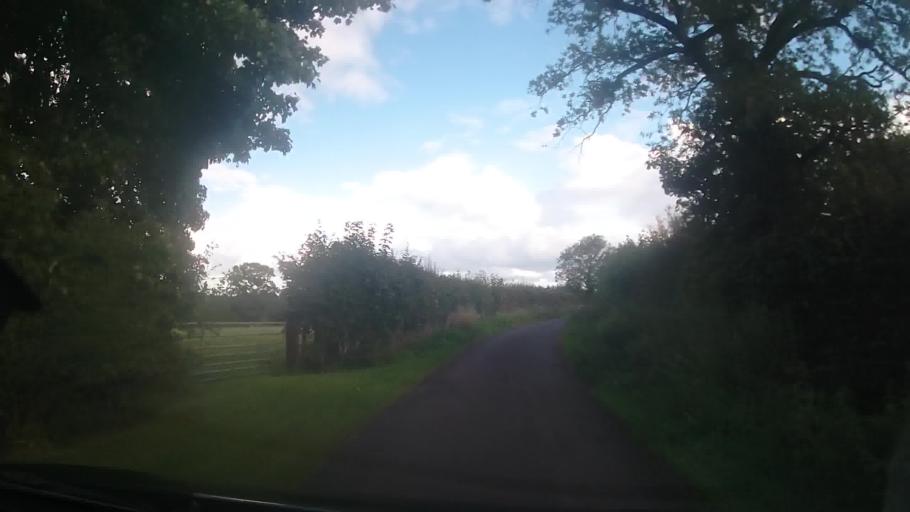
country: GB
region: England
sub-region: Shropshire
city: Wem
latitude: 52.8864
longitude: -2.7430
